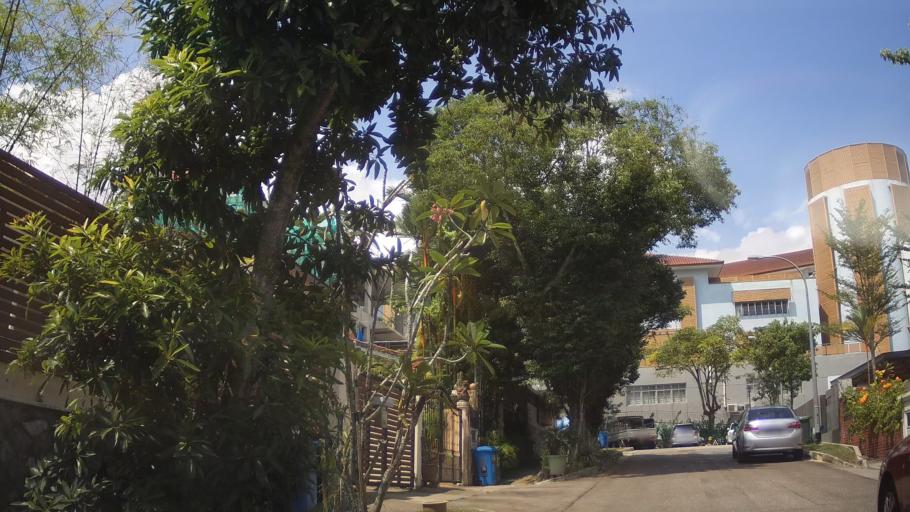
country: MY
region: Johor
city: Johor Bahru
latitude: 1.3681
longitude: 103.7705
